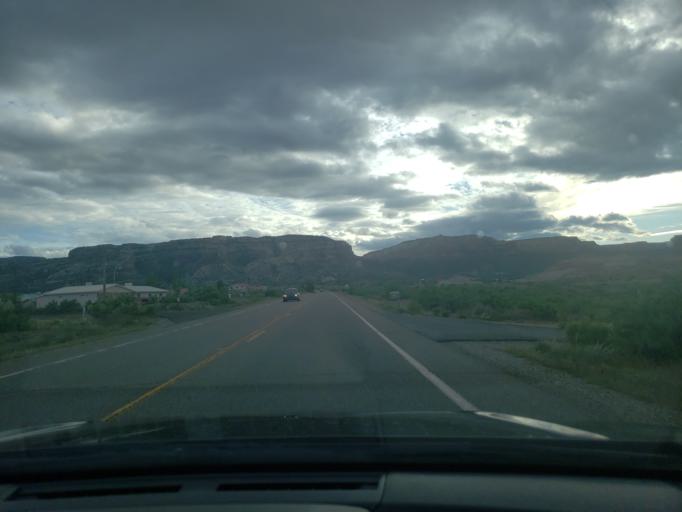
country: US
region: Colorado
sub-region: Mesa County
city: Redlands
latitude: 39.0466
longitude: -108.6185
